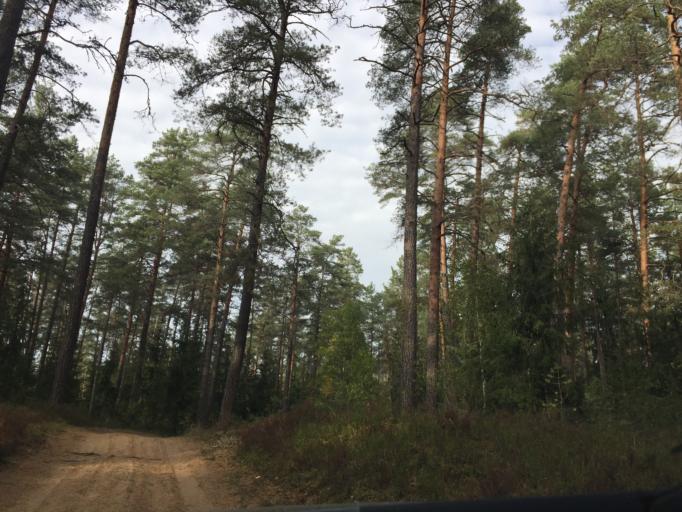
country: LV
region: Garkalne
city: Garkalne
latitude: 56.9477
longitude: 24.4300
